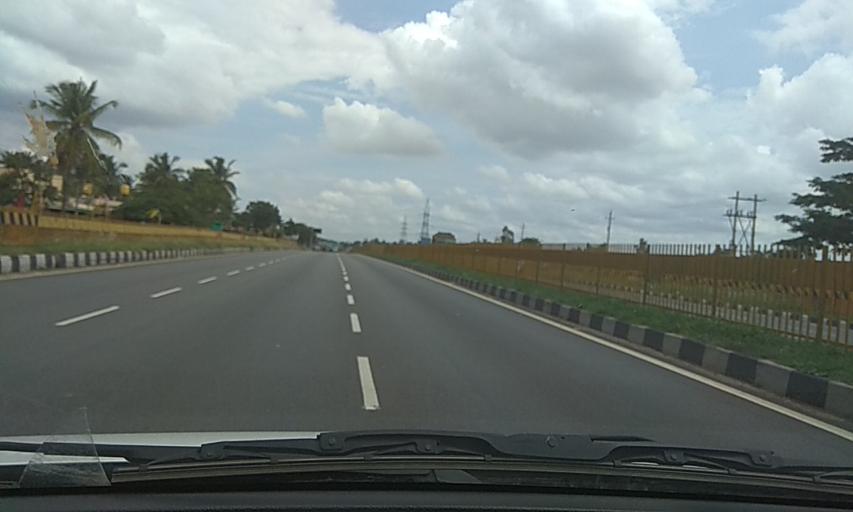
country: IN
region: Karnataka
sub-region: Tumkur
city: Tumkur
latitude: 13.3883
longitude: 77.0942
